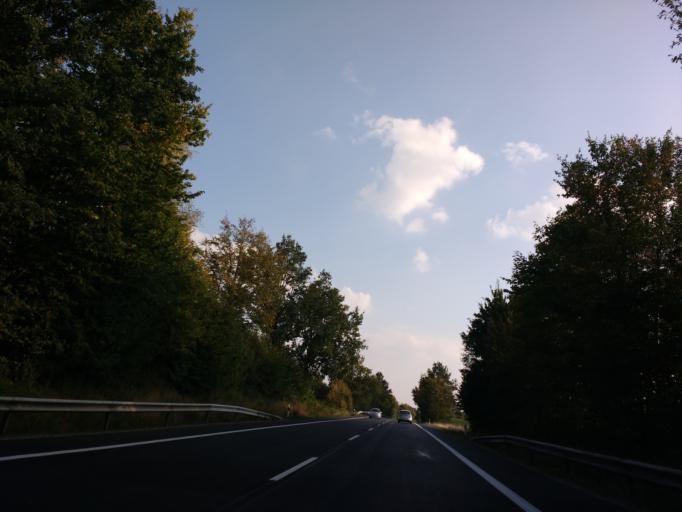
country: DE
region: North Rhine-Westphalia
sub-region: Regierungsbezirk Detmold
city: Blomberg
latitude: 51.9100
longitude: 9.0850
